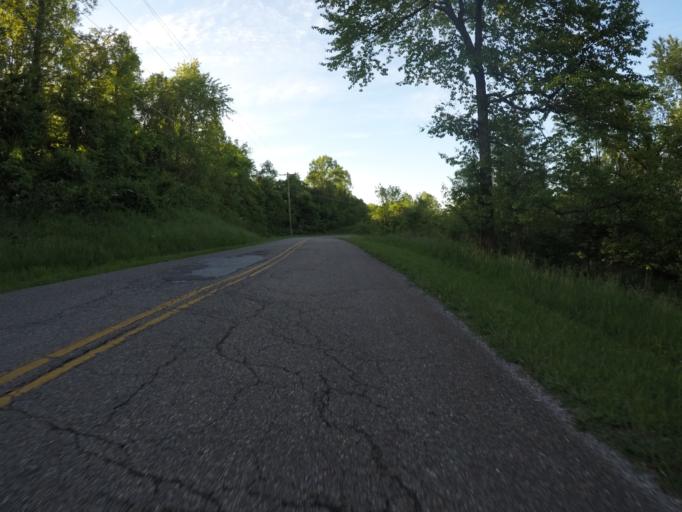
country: US
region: West Virginia
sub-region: Cabell County
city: Huntington
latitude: 38.5418
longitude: -82.4325
